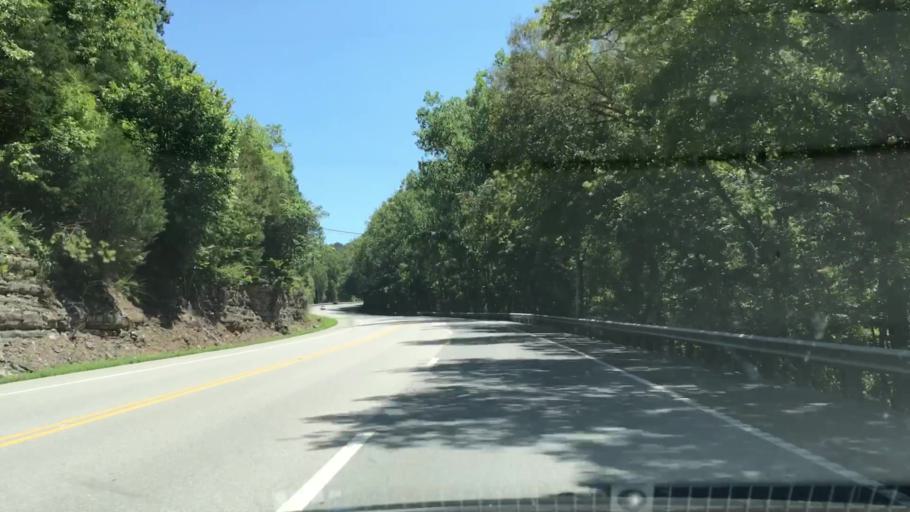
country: US
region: Tennessee
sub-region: Jackson County
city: Gainesboro
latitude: 36.3158
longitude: -85.6517
